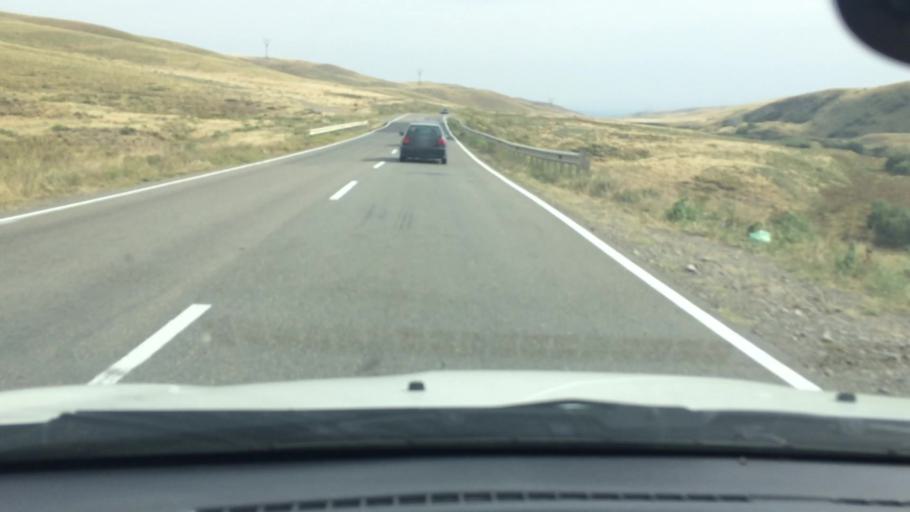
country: GE
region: Kvemo Kartli
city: Rust'avi
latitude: 41.5205
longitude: 44.9394
